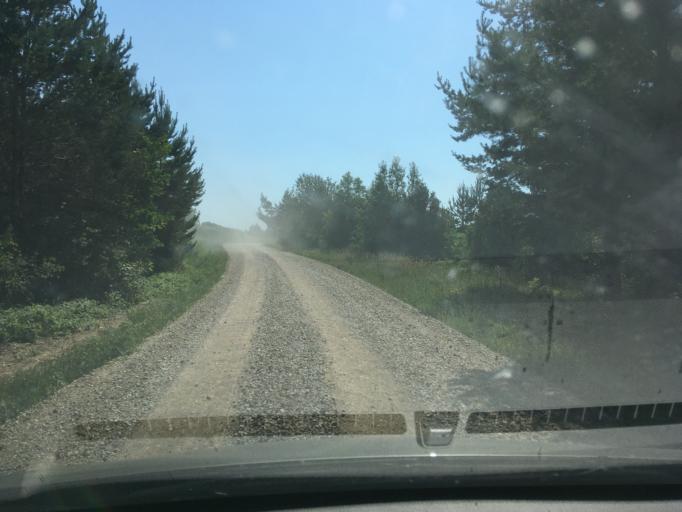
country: EE
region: Laeaene
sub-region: Lihula vald
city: Lihula
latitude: 58.5867
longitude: 23.7136
